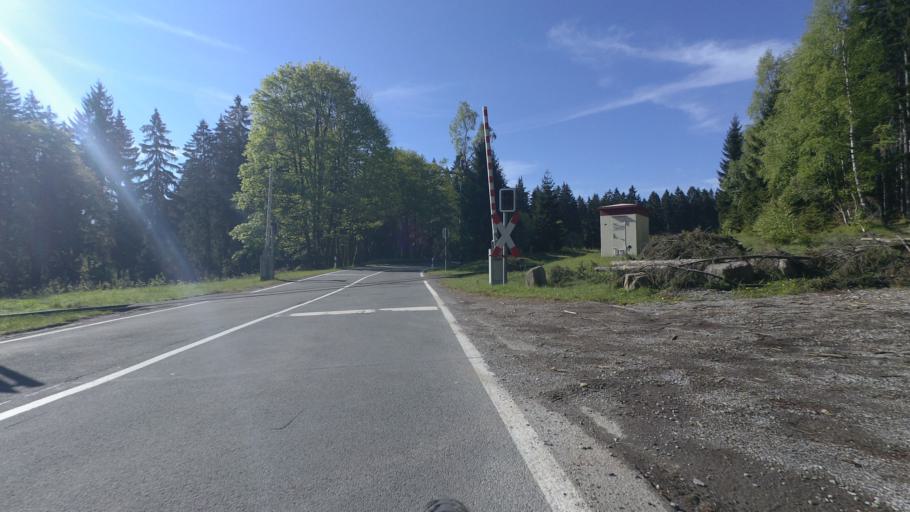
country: DE
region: Saxony-Anhalt
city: Darlingerode
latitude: 51.7679
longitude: 10.7217
